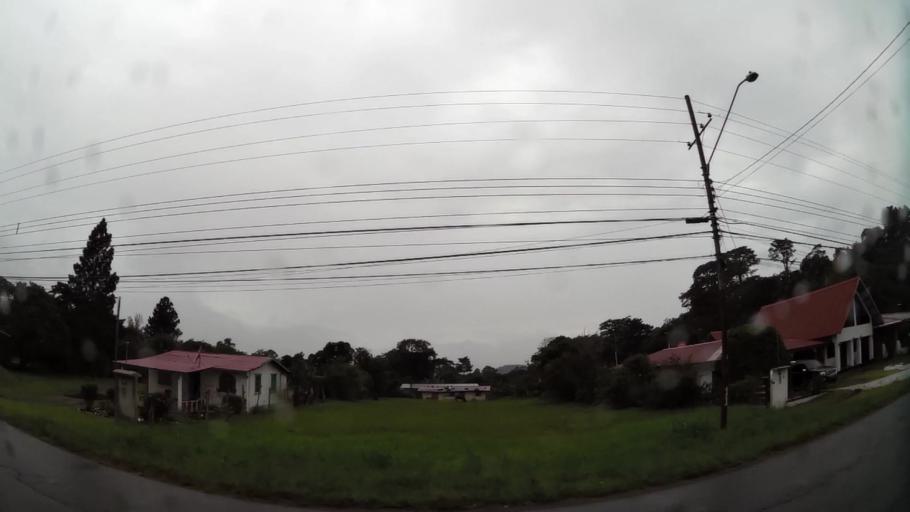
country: PA
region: Chiriqui
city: Volcan
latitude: 8.7731
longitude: -82.6374
